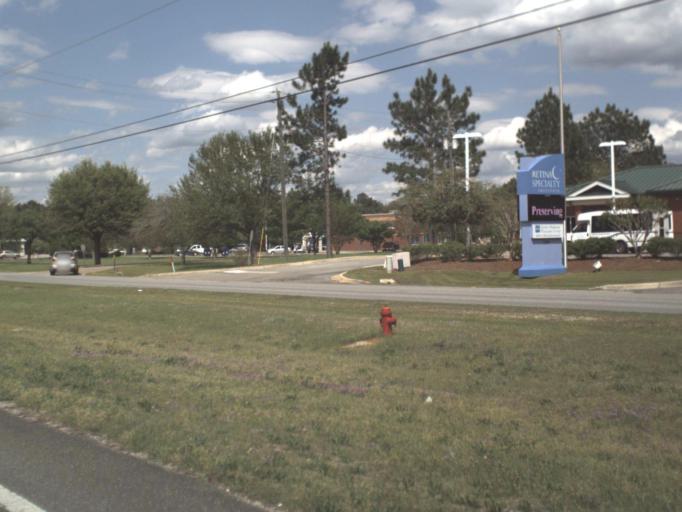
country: US
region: Florida
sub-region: Okaloosa County
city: Crestview
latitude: 30.7890
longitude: -86.5587
